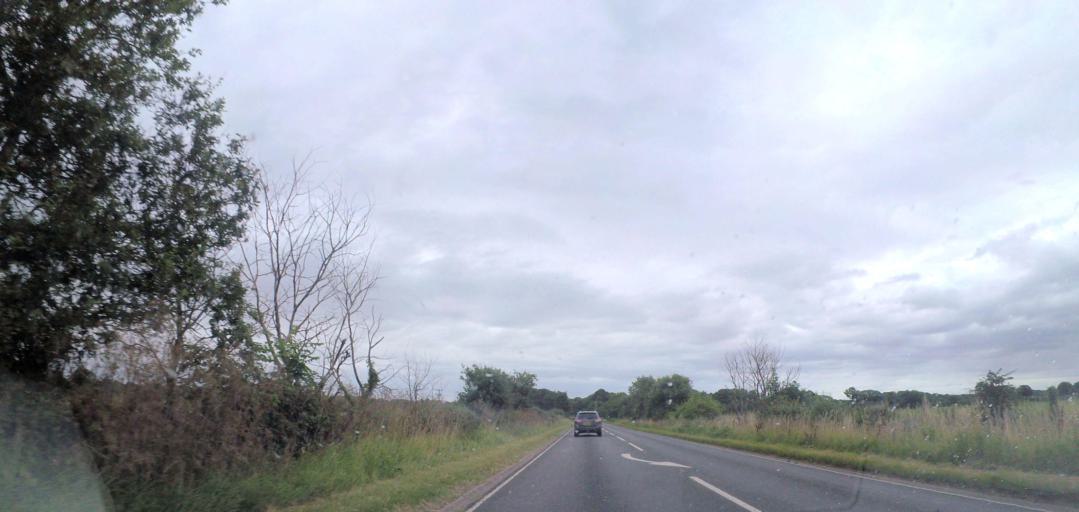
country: GB
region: England
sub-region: Norfolk
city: Spixworth
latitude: 52.6898
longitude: 1.3352
